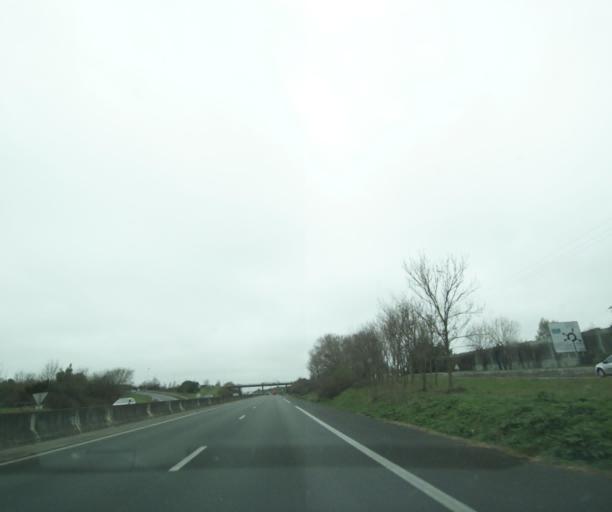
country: FR
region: Poitou-Charentes
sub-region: Departement de la Charente-Maritime
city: Perigny
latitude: 46.1512
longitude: -1.1124
